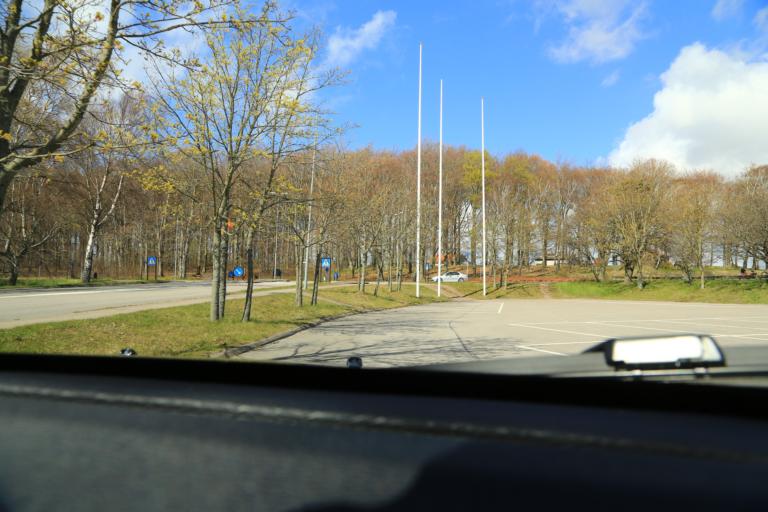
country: SE
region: Halland
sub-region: Varbergs Kommun
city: Varberg
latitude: 57.0997
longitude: 12.2621
